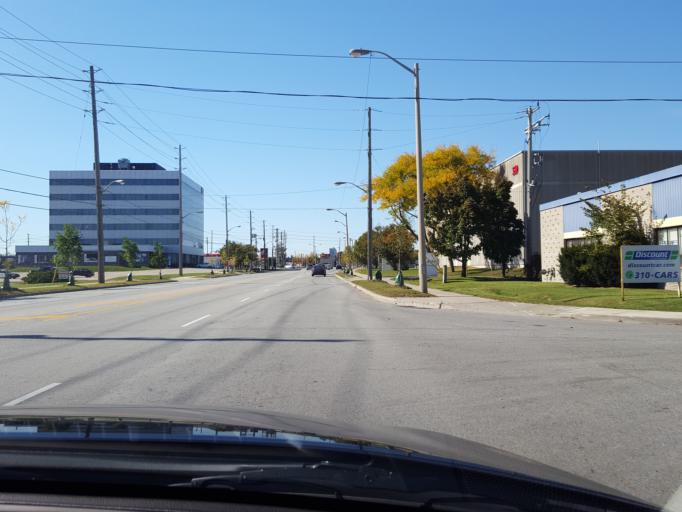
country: CA
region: Ontario
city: Etobicoke
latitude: 43.6166
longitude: -79.5209
